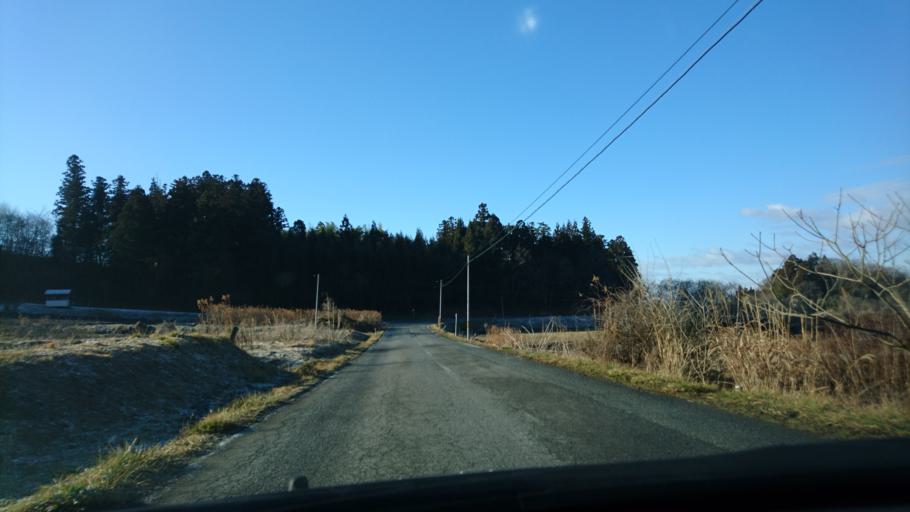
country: JP
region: Iwate
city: Ichinoseki
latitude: 38.8702
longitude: 141.2960
